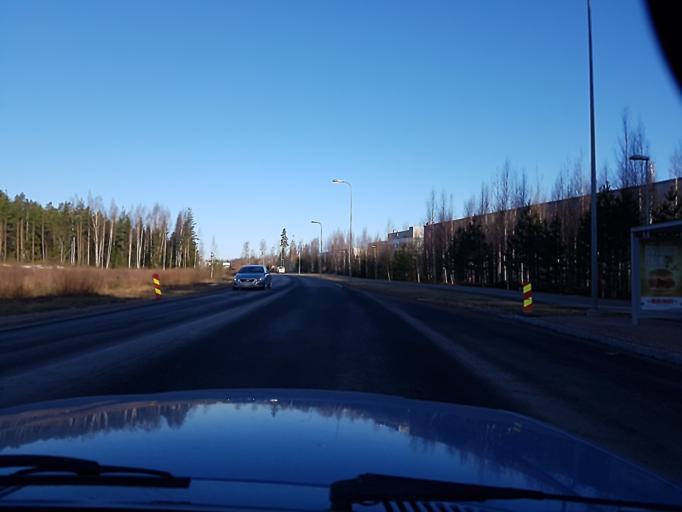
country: FI
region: Uusimaa
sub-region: Helsinki
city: Vantaa
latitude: 60.2926
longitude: 24.9303
